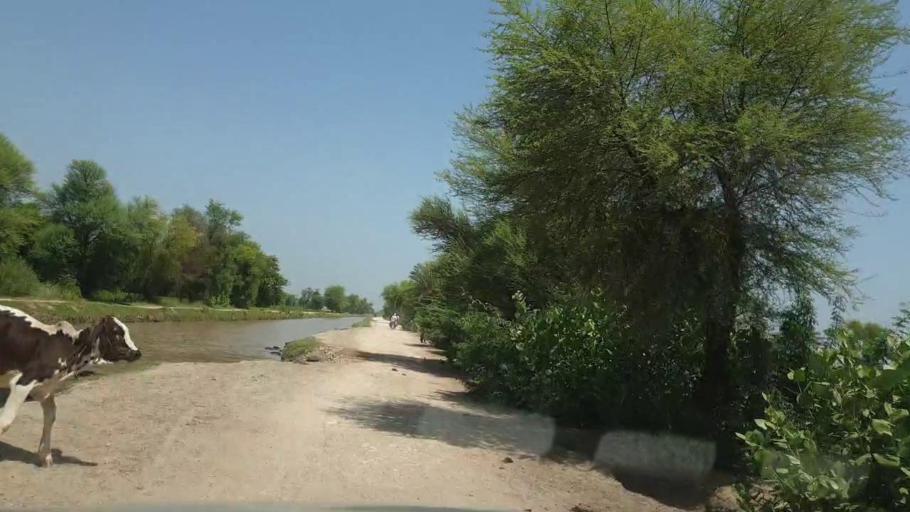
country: PK
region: Sindh
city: Pano Aqil
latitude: 27.6504
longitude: 69.1061
